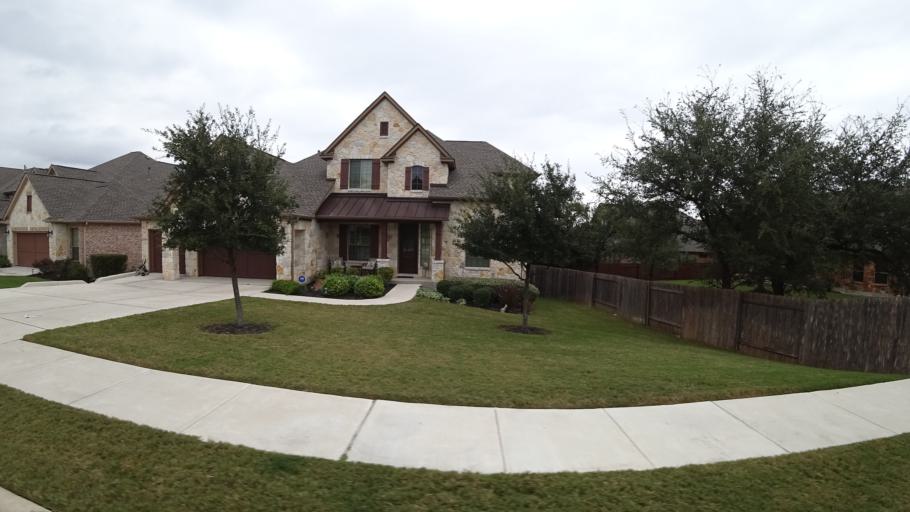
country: US
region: Texas
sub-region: Travis County
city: Bee Cave
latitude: 30.3420
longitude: -97.9031
